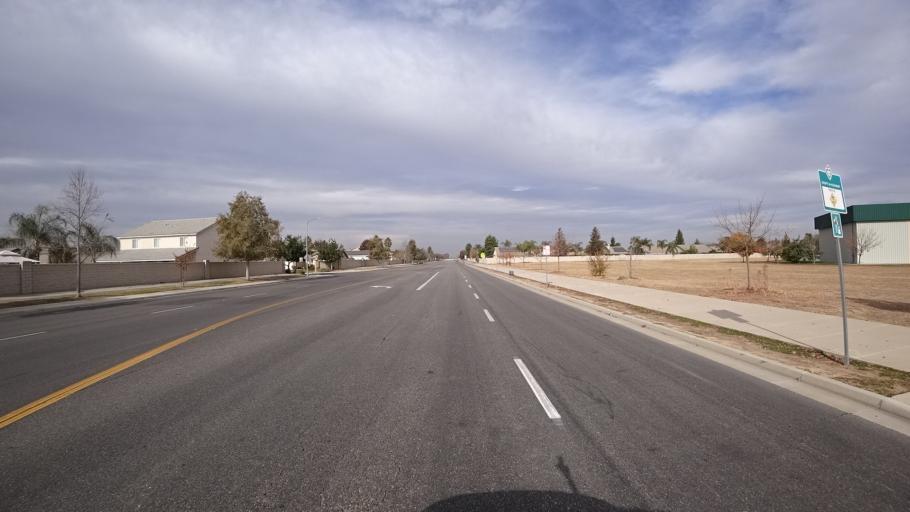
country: US
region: California
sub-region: Kern County
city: Rosedale
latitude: 35.4205
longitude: -119.1365
